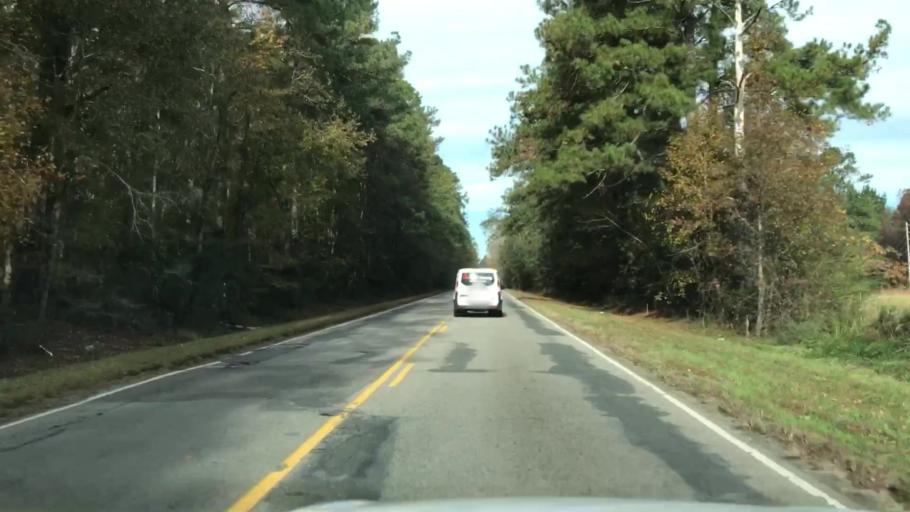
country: US
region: South Carolina
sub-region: Colleton County
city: Walterboro
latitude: 32.8866
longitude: -80.6225
